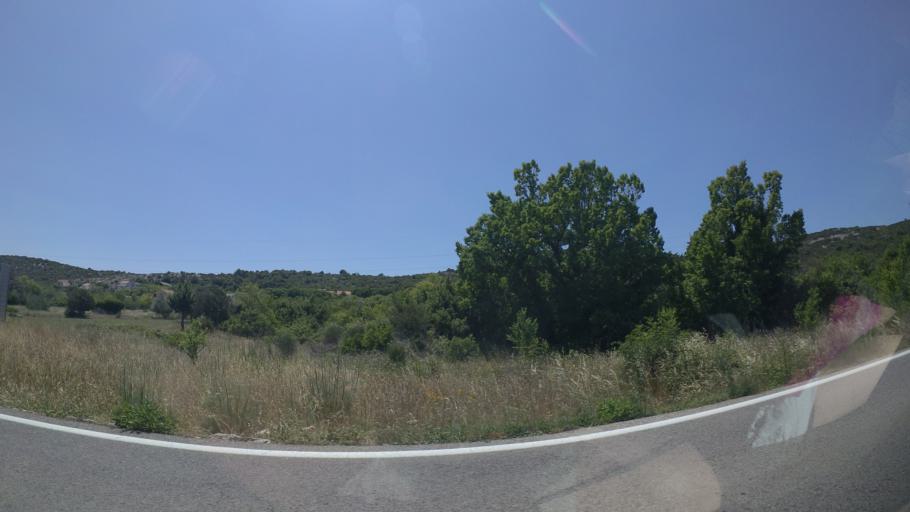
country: HR
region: Sibensko-Kniniska
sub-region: Grad Sibenik
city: Pirovac
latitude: 43.7974
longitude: 15.6791
